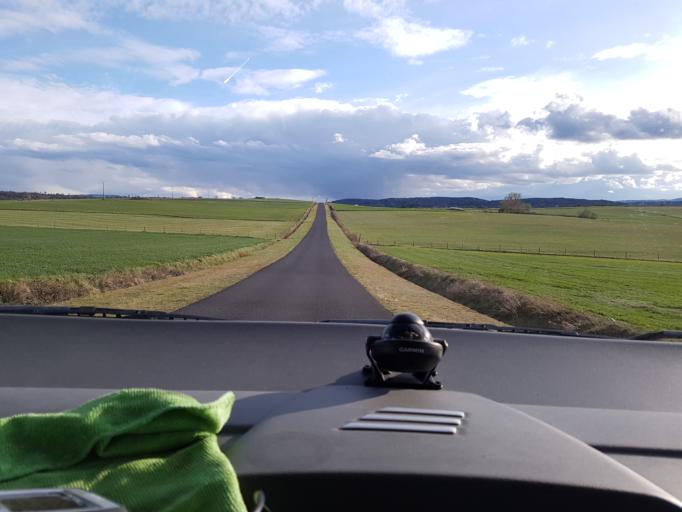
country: FR
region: Auvergne
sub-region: Departement de la Haute-Loire
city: Lempdes-sur-Allagnon
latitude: 45.3636
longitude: 3.2518
